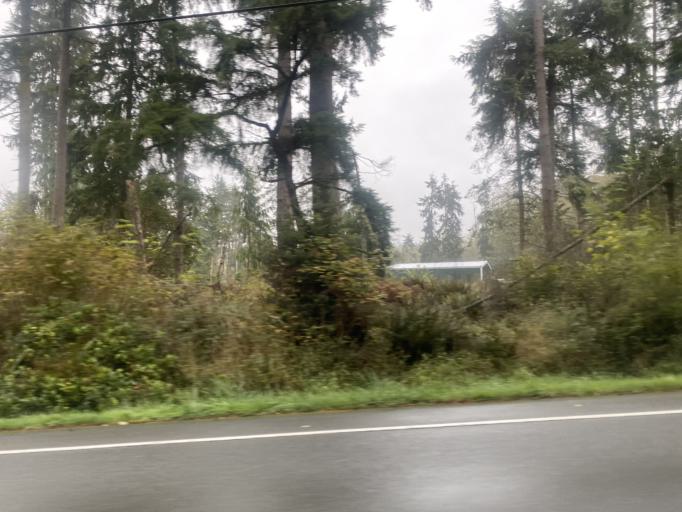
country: US
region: Washington
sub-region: Island County
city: Freeland
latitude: 48.0628
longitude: -122.5068
